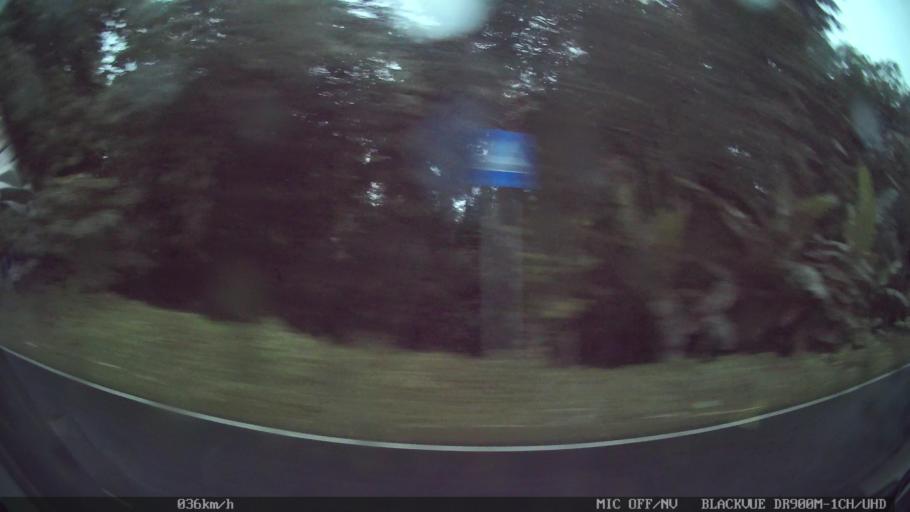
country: ID
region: Bali
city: Banjar Taro Kelod
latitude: -8.3577
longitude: 115.2753
